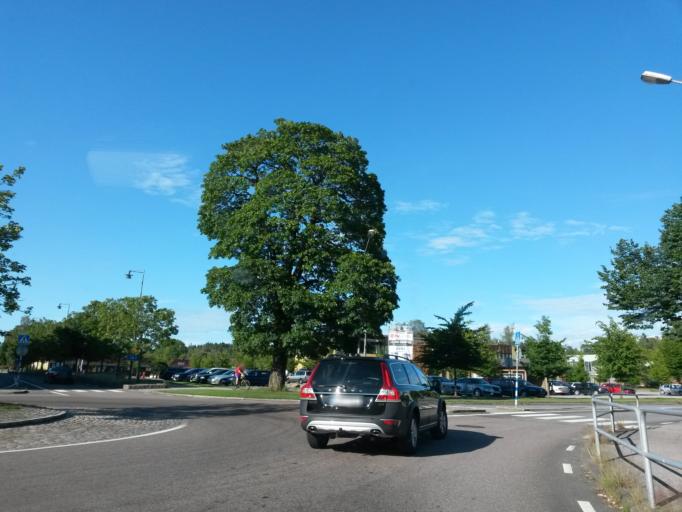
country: SE
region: Vaestra Goetaland
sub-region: Boras Kommun
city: Boras
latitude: 57.8249
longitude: 13.0090
